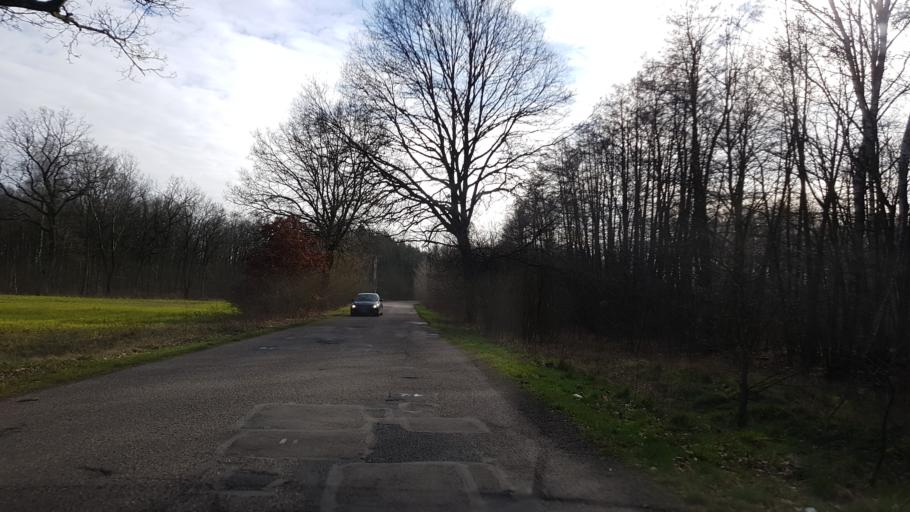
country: PL
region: West Pomeranian Voivodeship
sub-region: Powiat policki
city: Dobra
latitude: 53.5281
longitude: 14.3228
